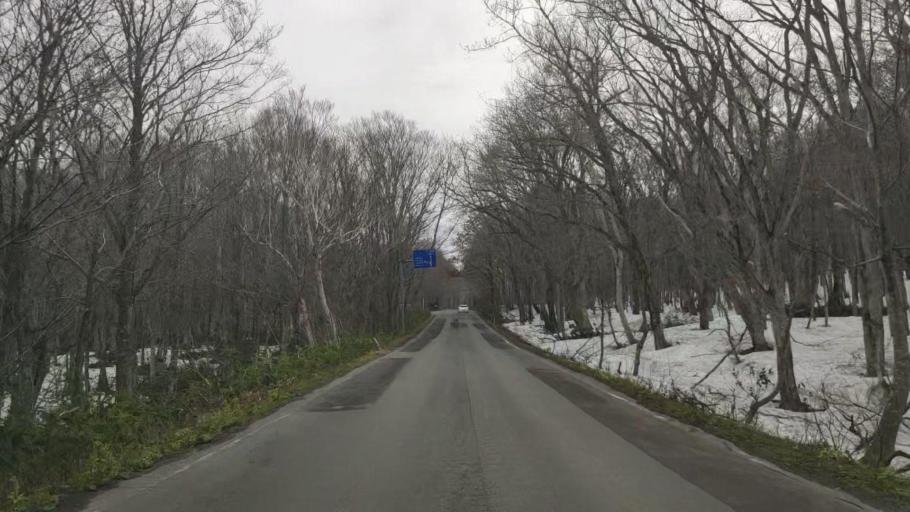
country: JP
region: Aomori
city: Aomori Shi
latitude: 40.6977
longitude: 140.9040
